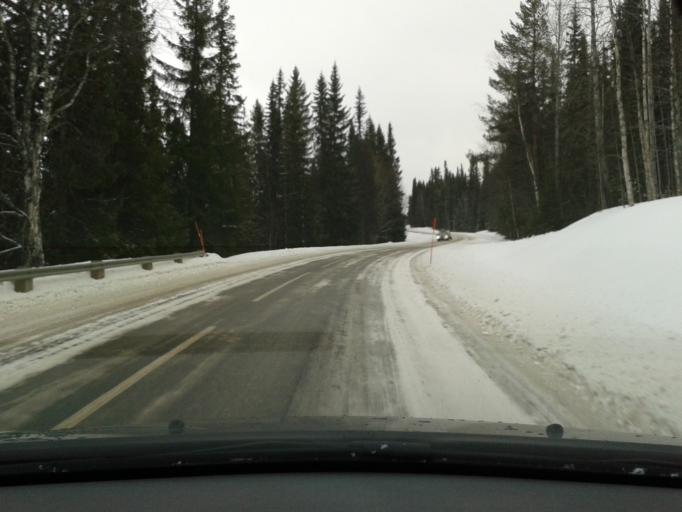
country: SE
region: Vaesterbotten
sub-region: Vilhelmina Kommun
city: Sjoberg
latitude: 64.6577
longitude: 16.3163
